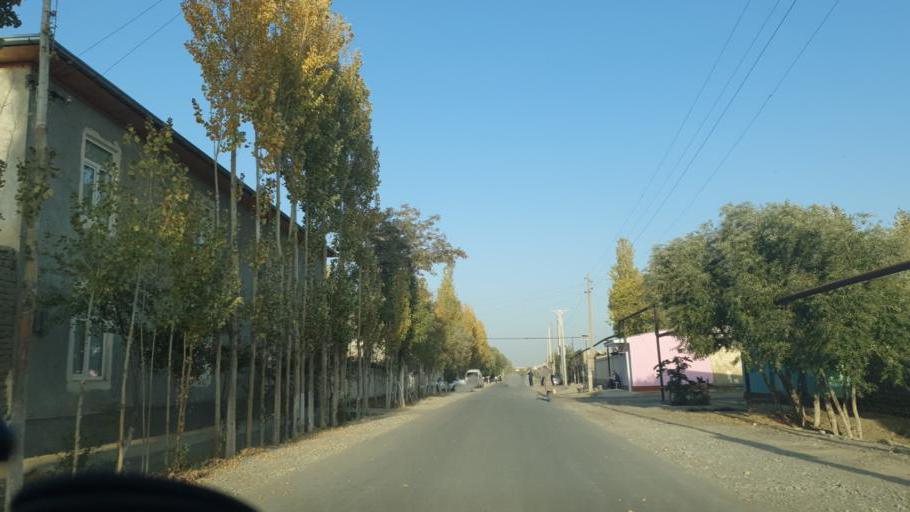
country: UZ
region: Fergana
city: Beshariq
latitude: 40.4661
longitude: 70.5564
